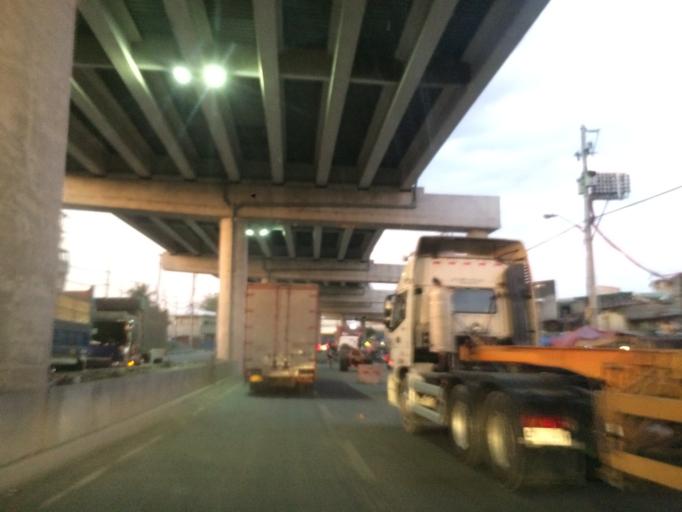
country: PH
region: Metro Manila
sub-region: Caloocan City
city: Niugan
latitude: 14.6433
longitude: 120.9616
